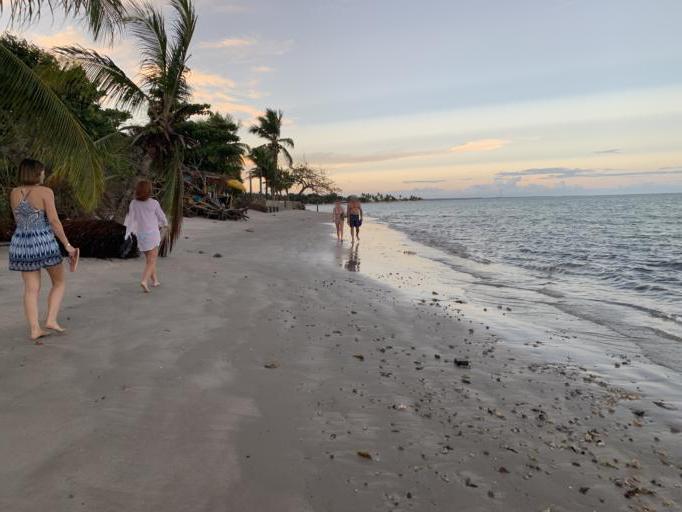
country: BR
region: Bahia
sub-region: Santa Cruz Cabralia
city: Santa Cruz Cabralia
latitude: -16.3419
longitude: -39.0061
